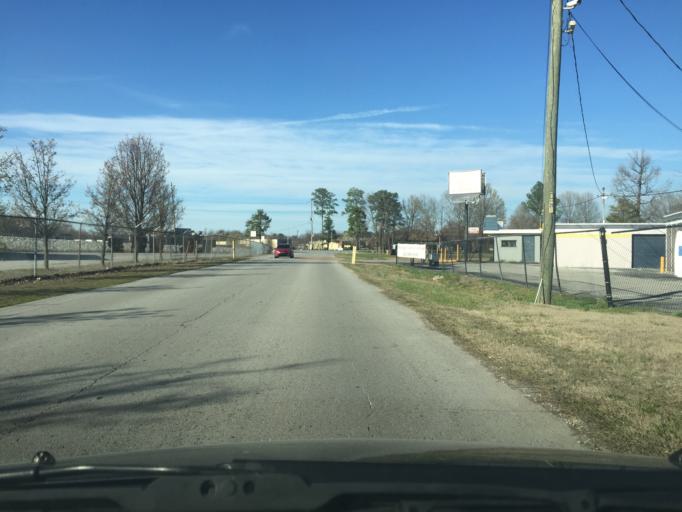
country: US
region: Tennessee
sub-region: Hamilton County
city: East Brainerd
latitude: 35.0256
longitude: -85.1908
